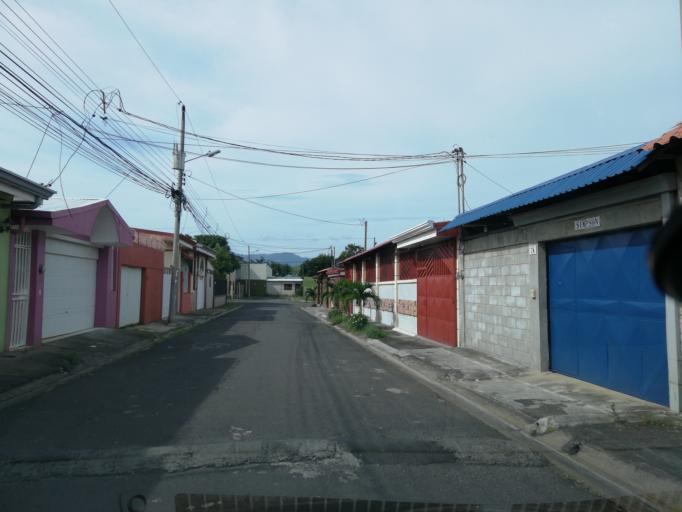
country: CR
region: Alajuela
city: Alajuela
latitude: 10.0104
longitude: -84.1976
